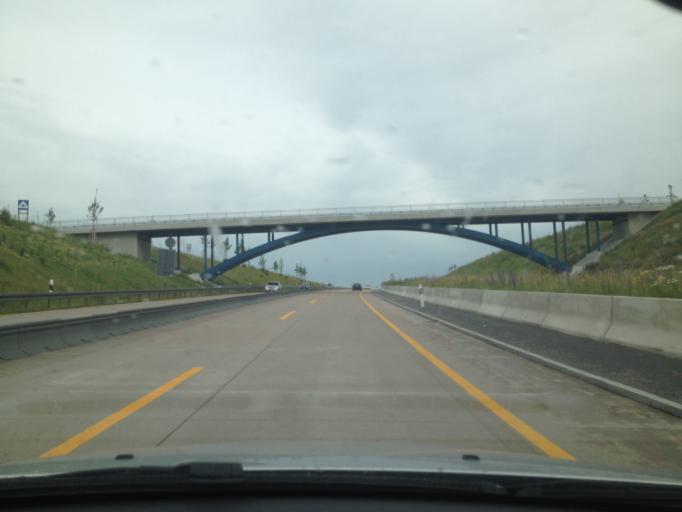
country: DE
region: Bavaria
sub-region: Swabia
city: Burgau
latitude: 48.4151
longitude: 10.4052
